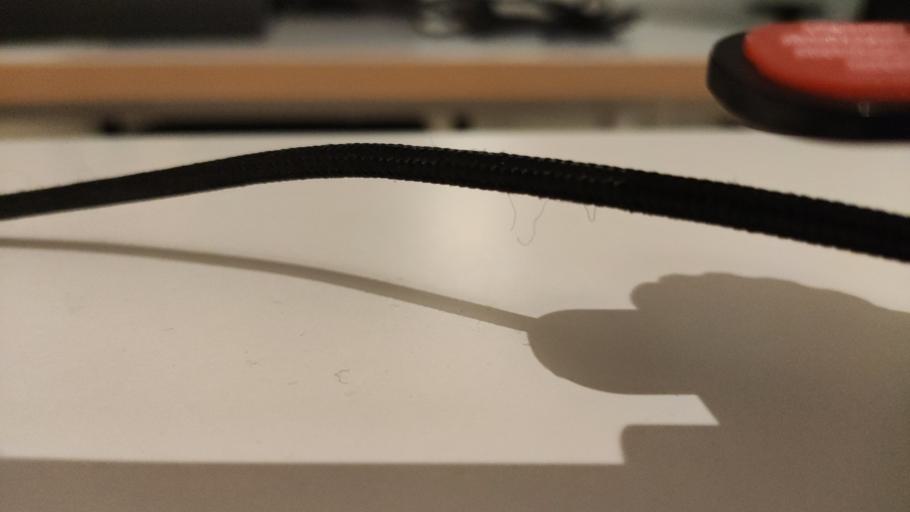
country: RU
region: Moskovskaya
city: Orekhovo-Zuyevo
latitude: 55.8346
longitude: 38.9693
